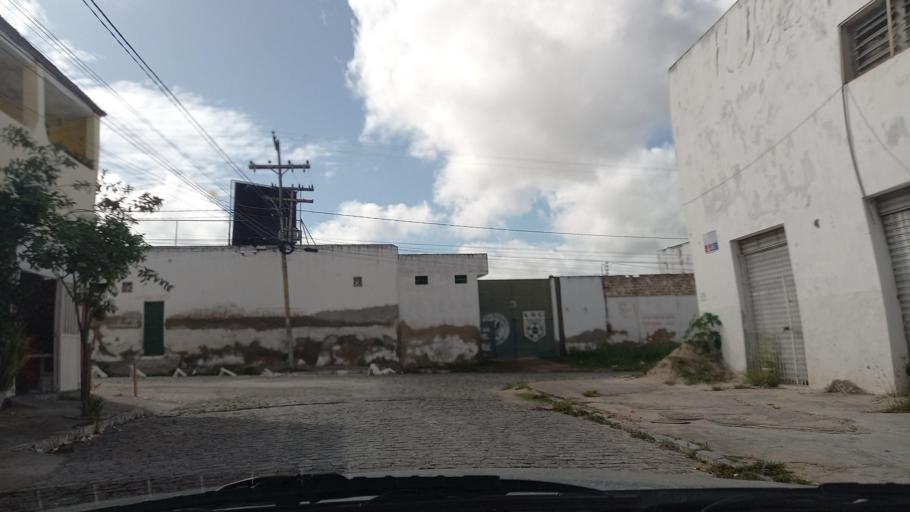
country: BR
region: Pernambuco
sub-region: Caruaru
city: Caruaru
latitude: -8.2908
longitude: -35.9816
